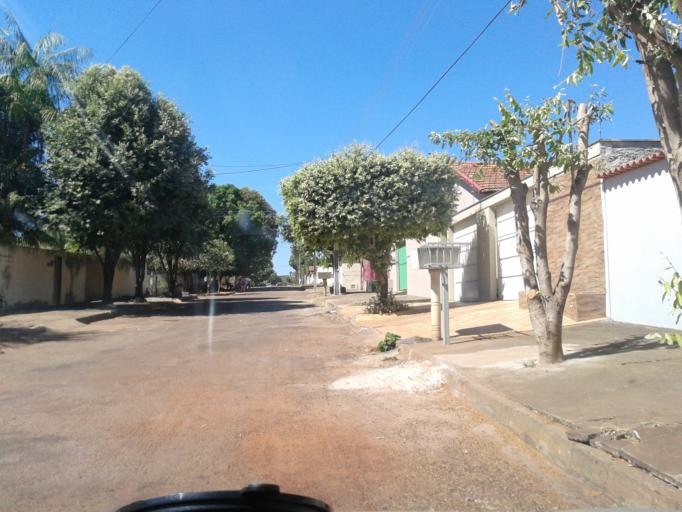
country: BR
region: Goias
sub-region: Sao Miguel Do Araguaia
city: Sao Miguel do Araguaia
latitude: -13.2805
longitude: -50.1563
